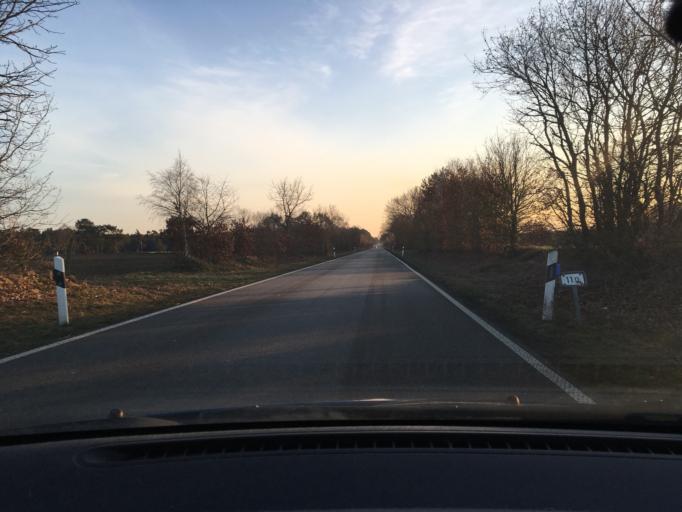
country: DE
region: Schleswig-Holstein
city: Besenthal
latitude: 53.5252
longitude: 10.7464
